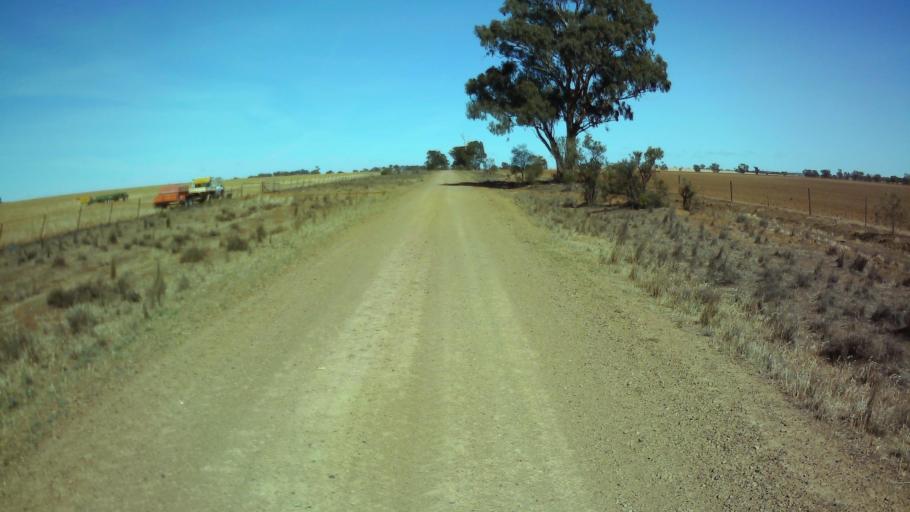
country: AU
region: New South Wales
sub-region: Weddin
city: Grenfell
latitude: -33.7501
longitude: 147.8937
